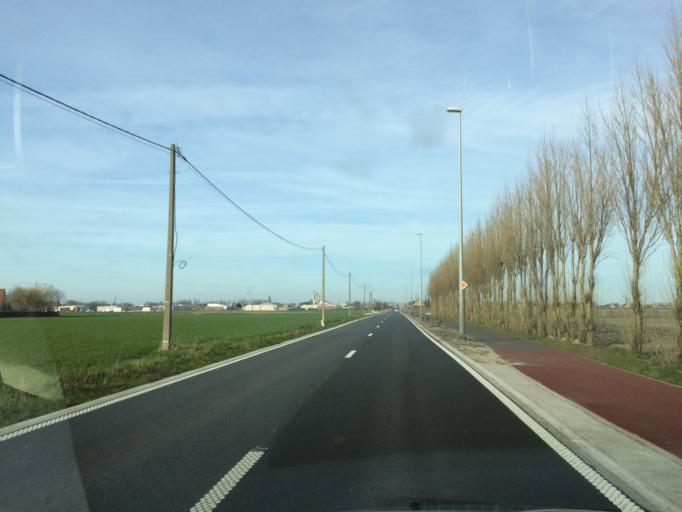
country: BE
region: Flanders
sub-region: Provincie West-Vlaanderen
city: Nieuwpoort
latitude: 51.1190
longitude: 2.7652
